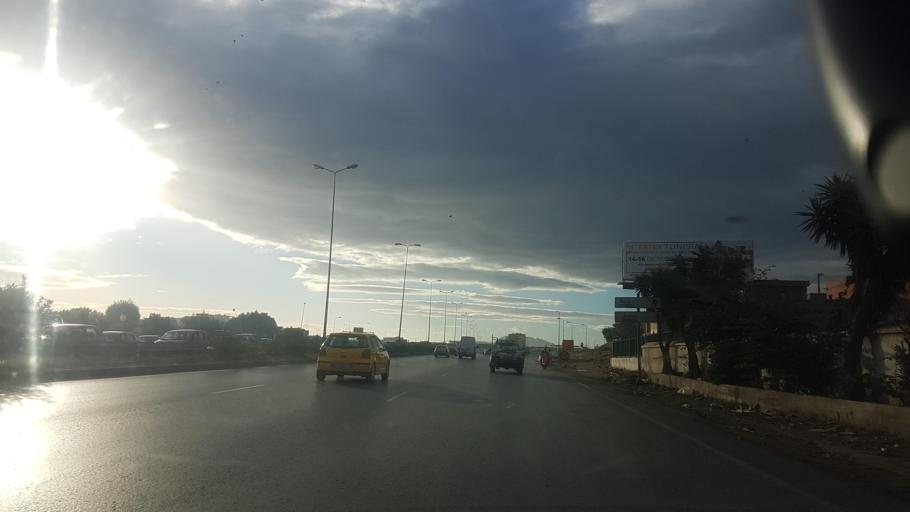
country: TN
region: Bin 'Arus
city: Ben Arous
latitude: 36.7497
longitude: 10.2066
